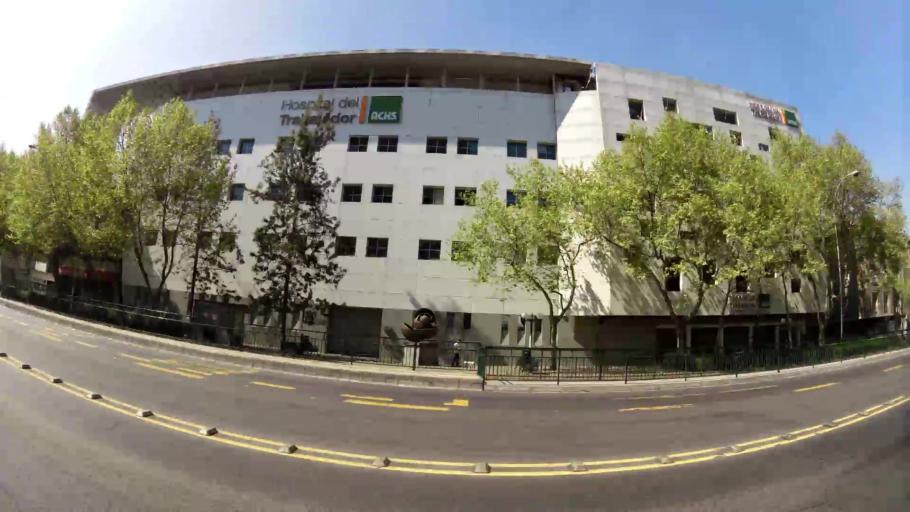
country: CL
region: Santiago Metropolitan
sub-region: Provincia de Santiago
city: Santiago
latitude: -33.4441
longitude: -70.6332
